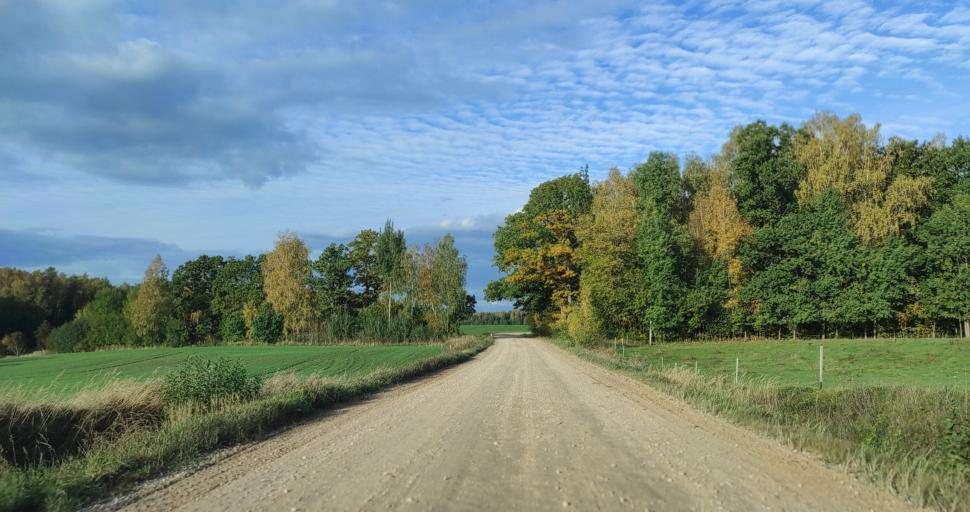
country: LV
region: Skrunda
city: Skrunda
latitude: 56.7433
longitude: 21.8450
